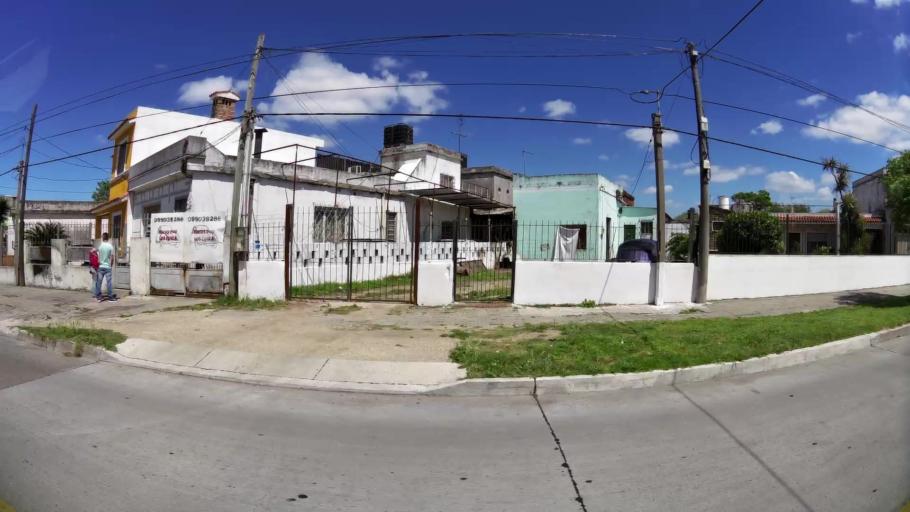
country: UY
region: Montevideo
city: Montevideo
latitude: -34.8579
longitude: -56.1348
